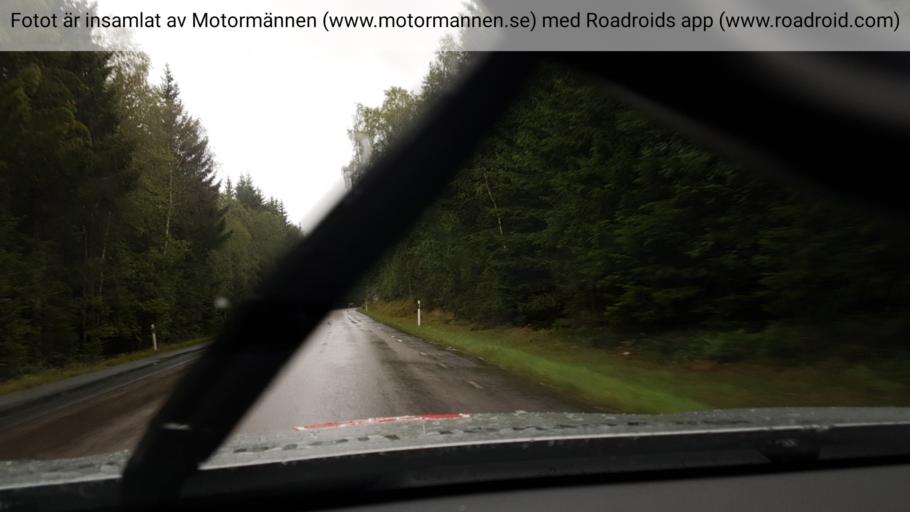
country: SE
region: Vaestra Goetaland
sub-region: Harryda Kommun
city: Hindas
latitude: 57.6958
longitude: 12.3843
